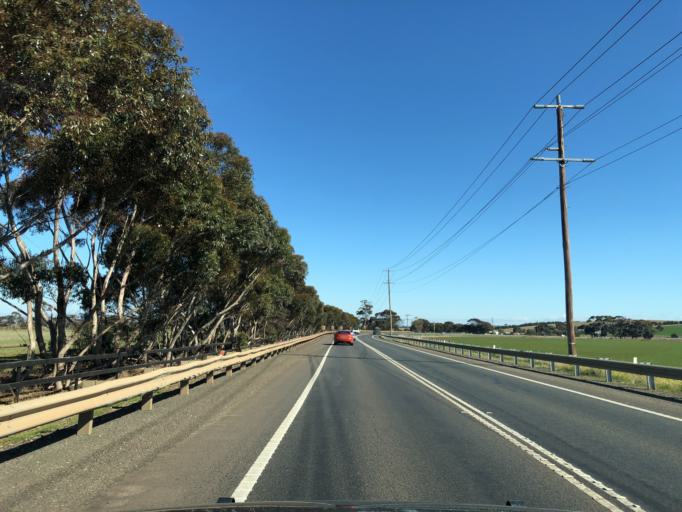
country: AU
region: Victoria
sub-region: Hume
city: Diggers Rest
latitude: -37.6258
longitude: 144.6487
